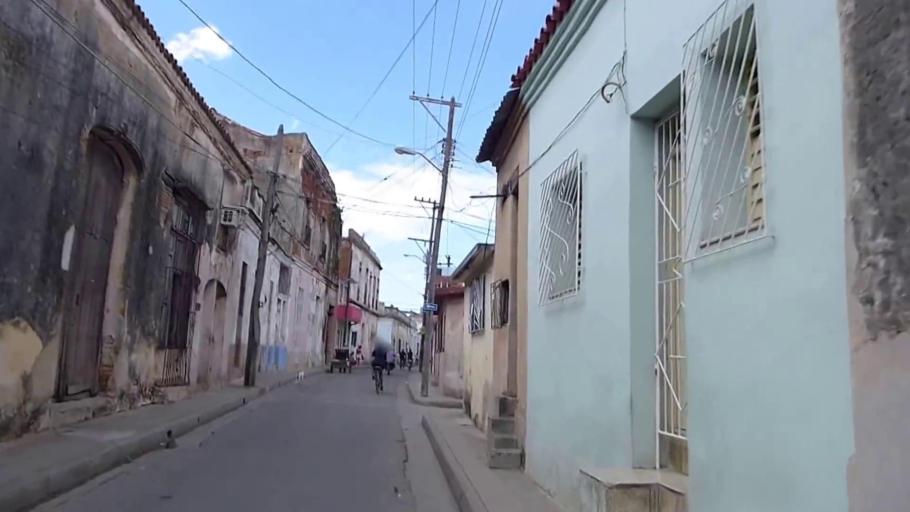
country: CU
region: Camaguey
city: Camaguey
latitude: 21.3862
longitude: -77.9191
